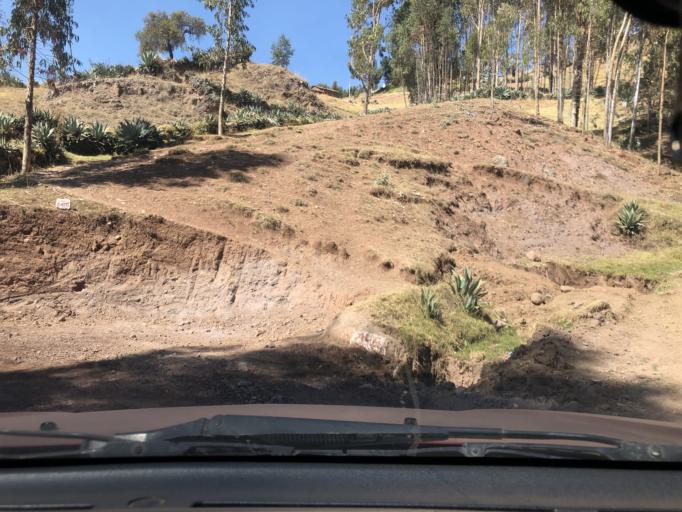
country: PE
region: Ayacucho
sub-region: Provincia de La Mar
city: Chilcas
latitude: -13.1697
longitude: -73.8500
